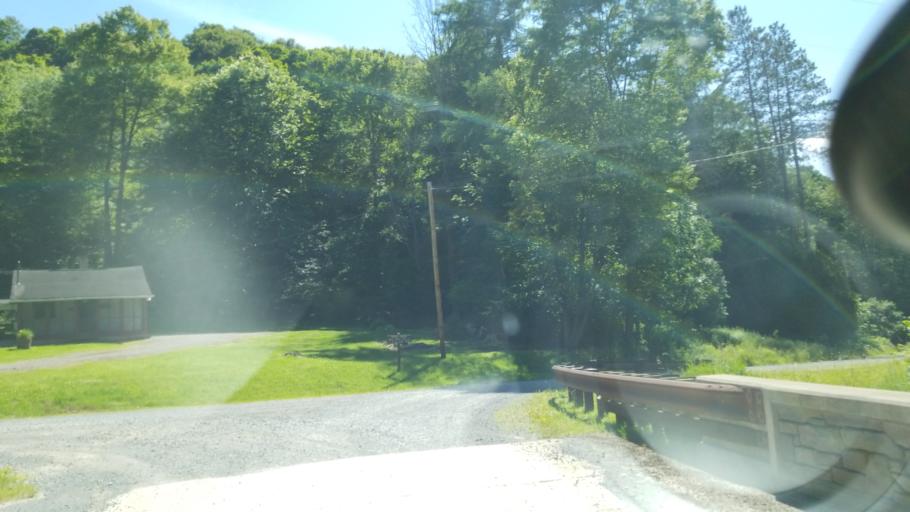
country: US
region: Pennsylvania
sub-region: Clearfield County
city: Clearfield
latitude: 41.2201
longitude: -78.3918
